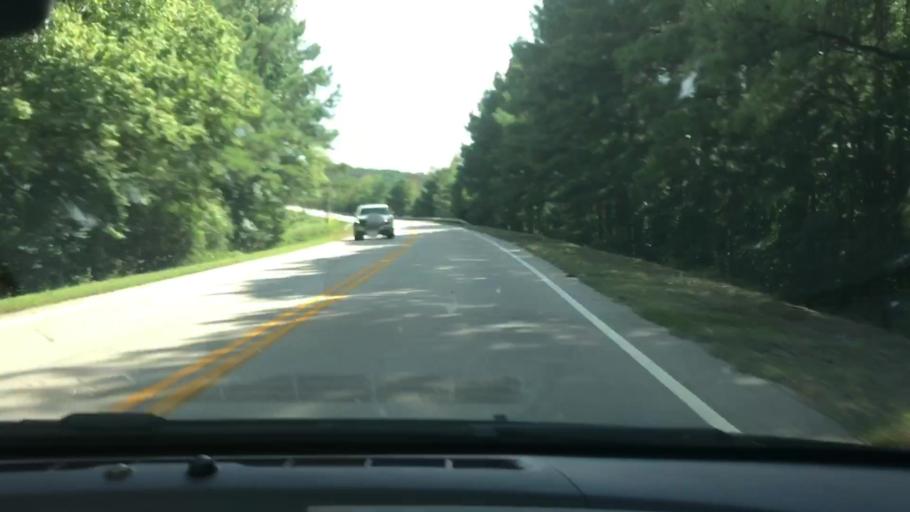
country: US
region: Georgia
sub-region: Troup County
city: La Grange
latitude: 33.1370
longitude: -85.0896
